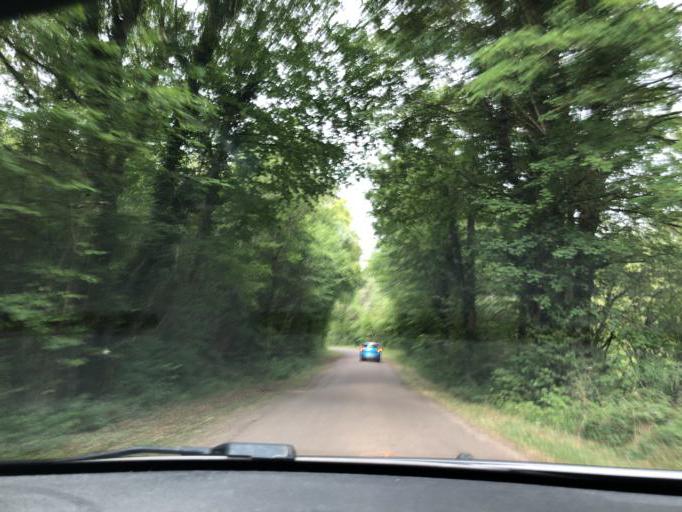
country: FR
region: Bourgogne
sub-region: Departement de l'Yonne
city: Chablis
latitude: 47.7788
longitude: 3.8213
